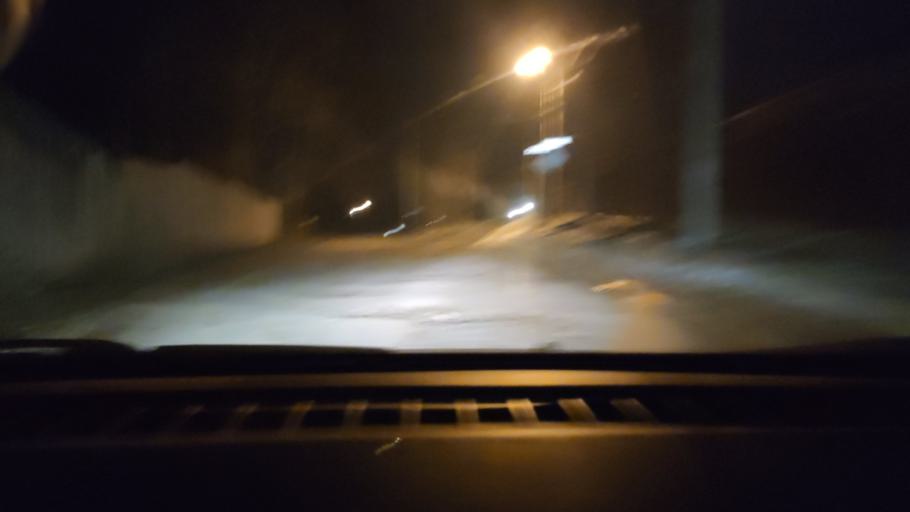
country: RU
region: Perm
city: Perm
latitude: 58.0820
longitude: 56.3556
